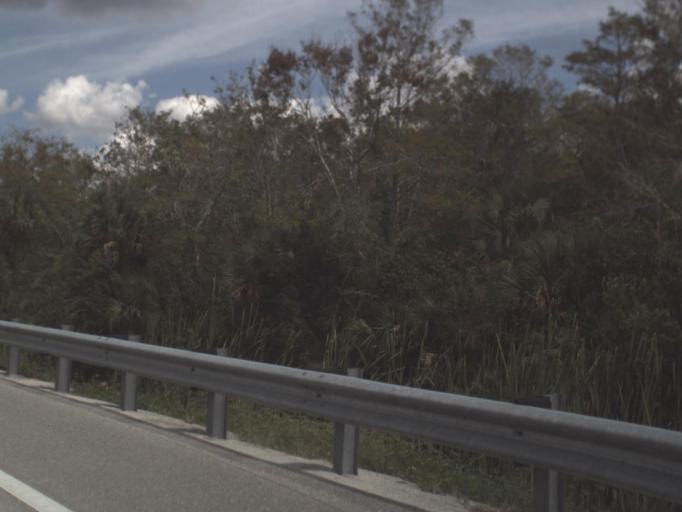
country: US
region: Florida
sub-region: Collier County
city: Marco
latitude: 25.9218
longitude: -81.3582
